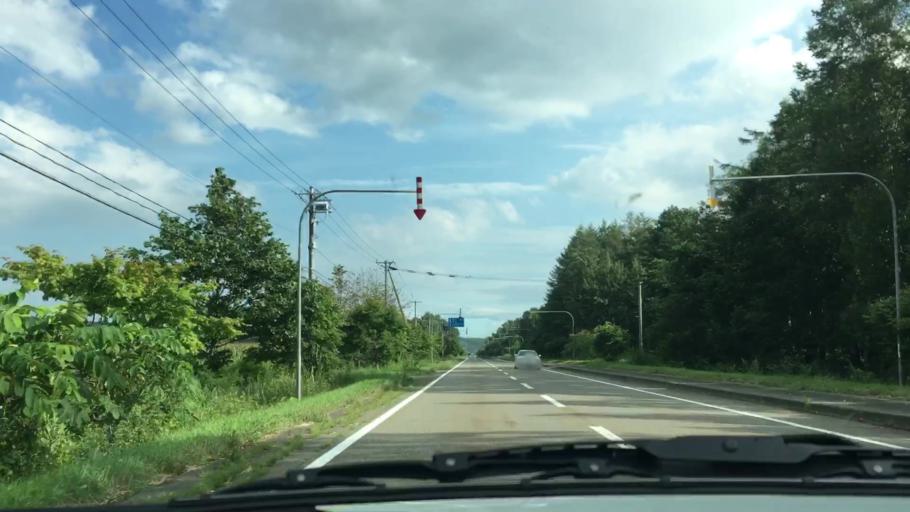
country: JP
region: Hokkaido
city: Otofuke
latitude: 43.3213
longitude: 143.3018
